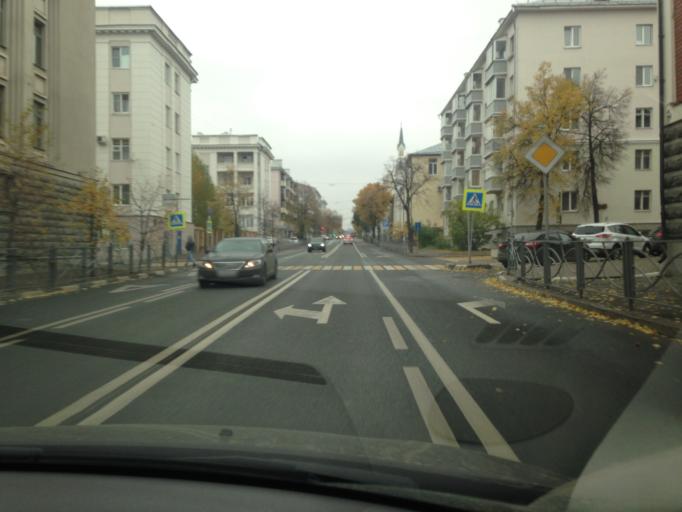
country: RU
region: Tatarstan
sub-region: Gorod Kazan'
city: Kazan
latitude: 55.7968
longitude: 49.1185
